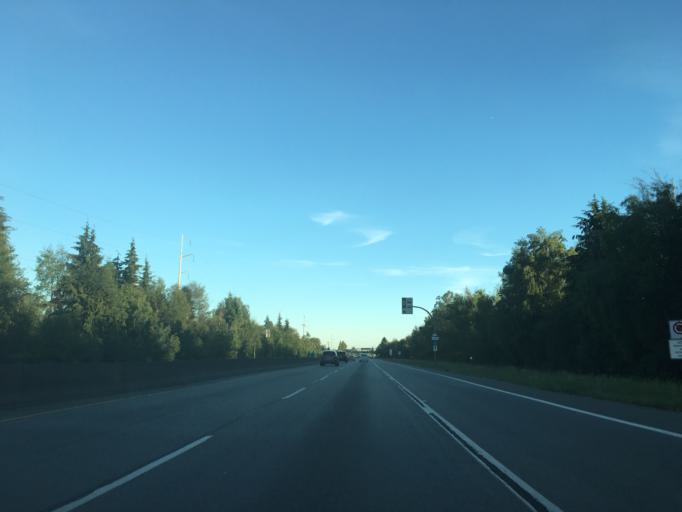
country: CA
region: British Columbia
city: Richmond
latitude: 49.1607
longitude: -123.0868
